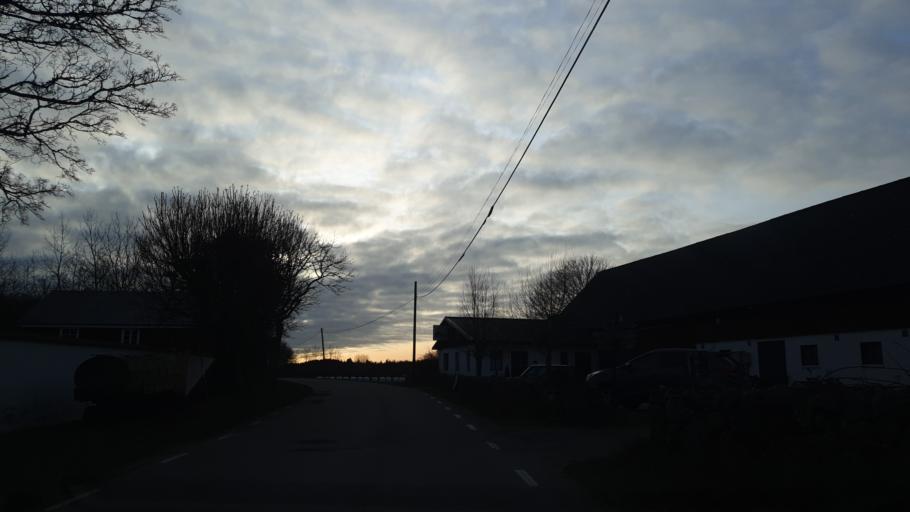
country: SE
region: Blekinge
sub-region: Karlskrona Kommun
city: Jaemjoe
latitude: 56.1893
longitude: 15.9458
